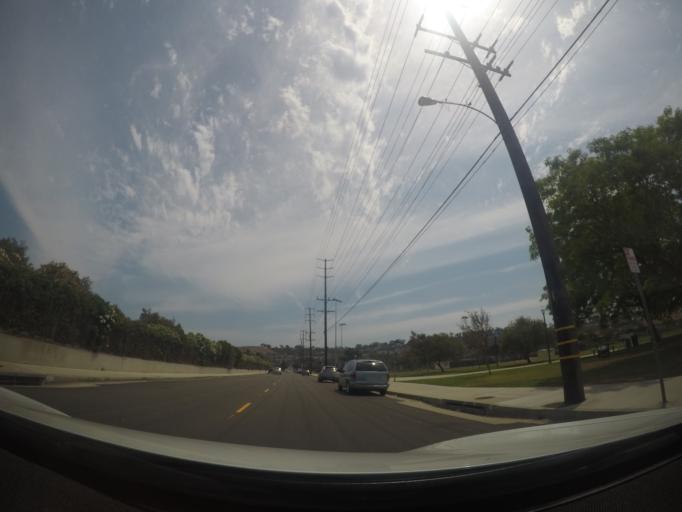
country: US
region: California
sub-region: Los Angeles County
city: Rolling Hills Estates
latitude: 33.8110
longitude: -118.3545
